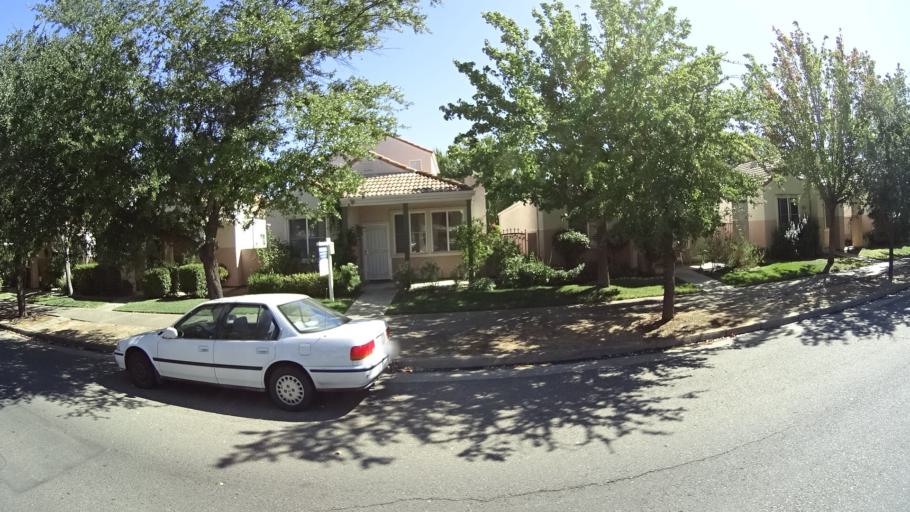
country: US
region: California
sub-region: Sacramento County
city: Laguna
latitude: 38.4258
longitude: -121.4660
